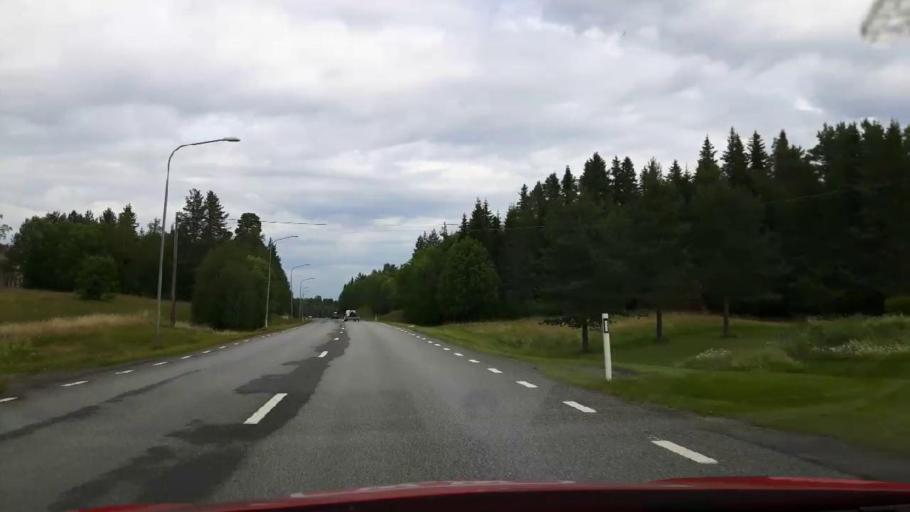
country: SE
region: Jaemtland
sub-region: Stroemsunds Kommun
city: Stroemsund
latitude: 63.6662
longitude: 15.3911
